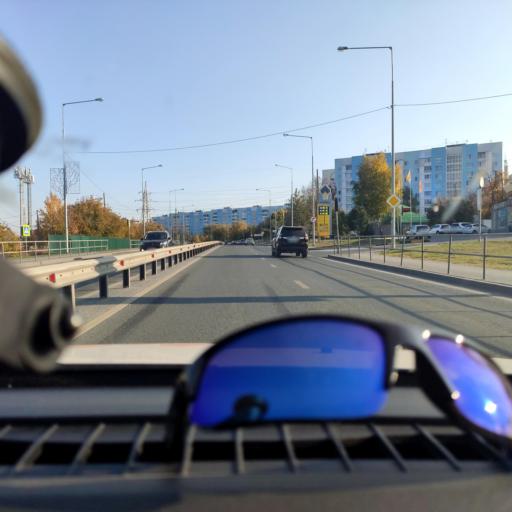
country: RU
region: Samara
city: Volzhskiy
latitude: 53.3547
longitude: 50.2106
